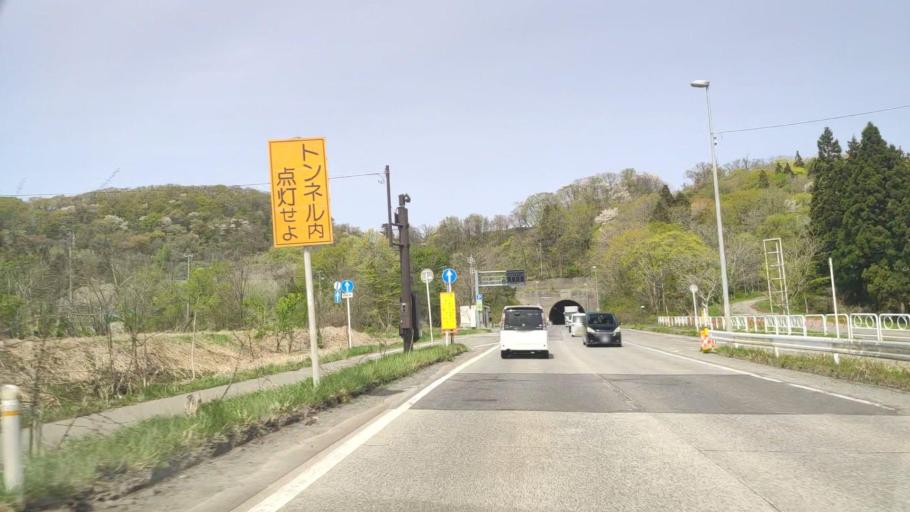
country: JP
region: Aomori
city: Aomori Shi
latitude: 40.8545
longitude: 140.8391
